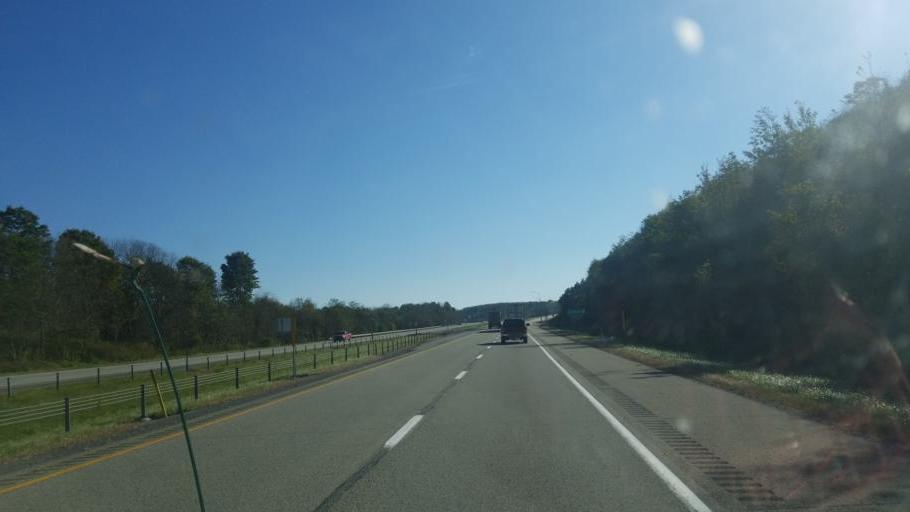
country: US
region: Pennsylvania
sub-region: Cambria County
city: Gallitzin
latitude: 40.4676
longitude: -78.5568
